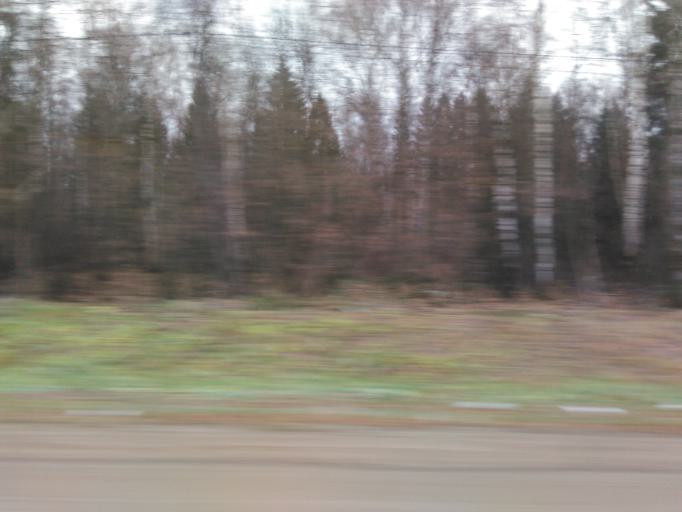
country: RU
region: Moskovskaya
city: Ashukino
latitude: 56.1472
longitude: 37.9882
